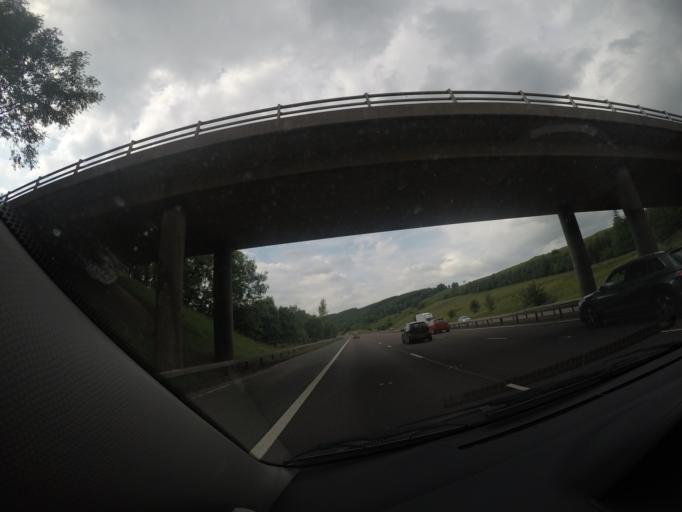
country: GB
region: Scotland
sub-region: Dumfries and Galloway
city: Moffat
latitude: 55.3365
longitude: -3.4823
